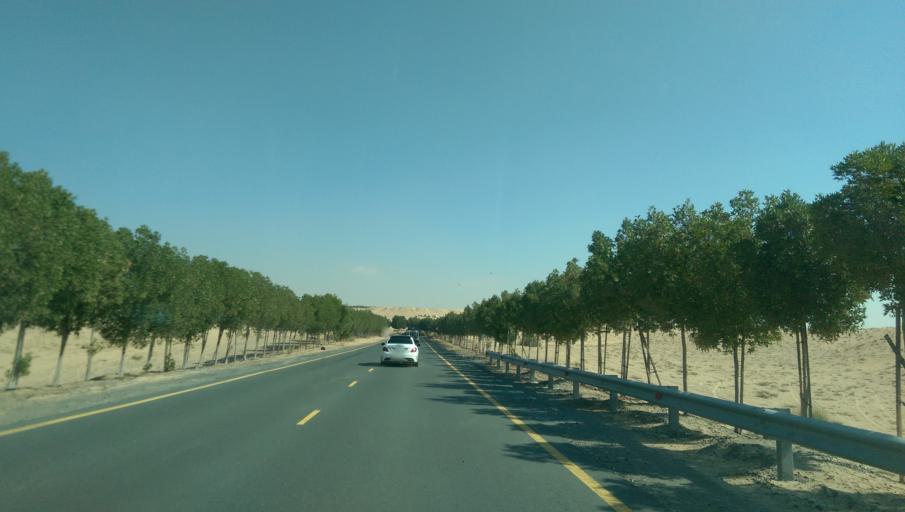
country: AE
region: Dubai
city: Dubai
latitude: 24.9861
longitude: 55.3470
